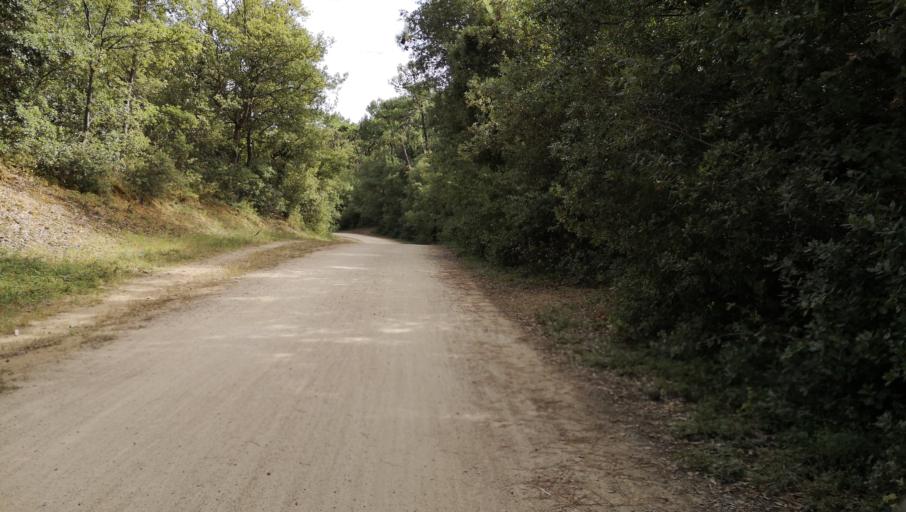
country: FR
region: Pays de la Loire
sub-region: Departement de la Vendee
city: Les Sables-d'Olonne
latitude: 46.5200
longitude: -1.8131
